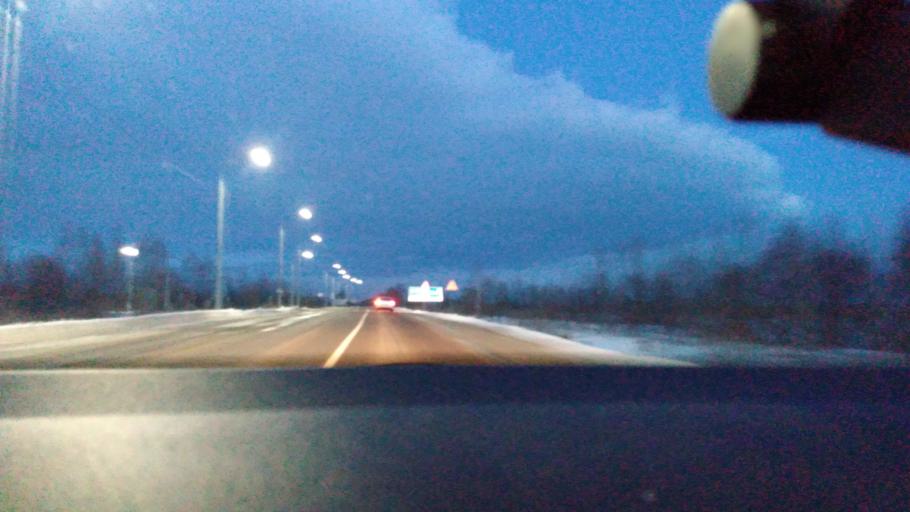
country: RU
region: Moskovskaya
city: Krasnaya Poyma
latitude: 55.1675
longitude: 39.1557
